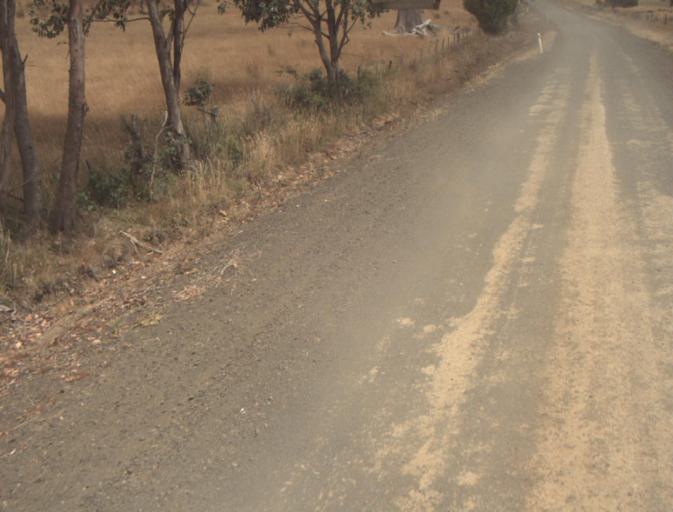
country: AU
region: Tasmania
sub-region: Northern Midlands
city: Evandale
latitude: -41.5215
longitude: 147.3856
